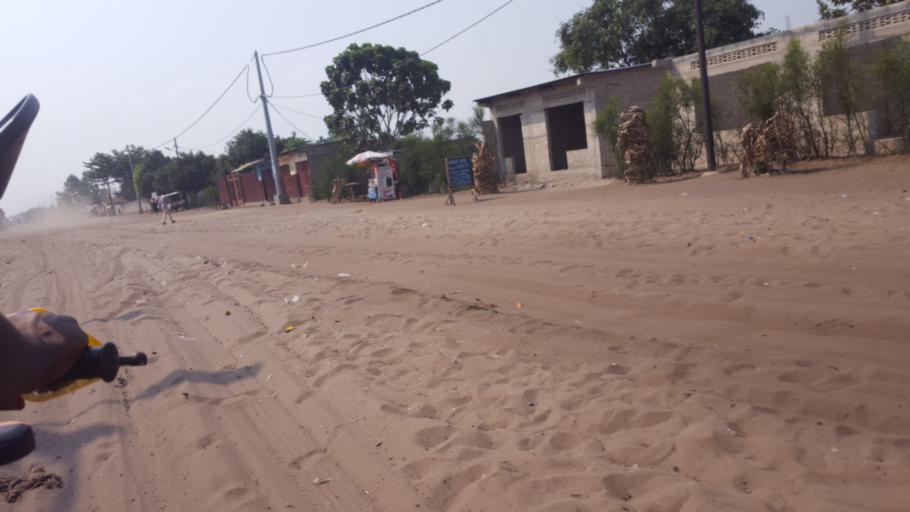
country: CD
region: Kinshasa
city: Masina
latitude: -4.3661
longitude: 15.5126
